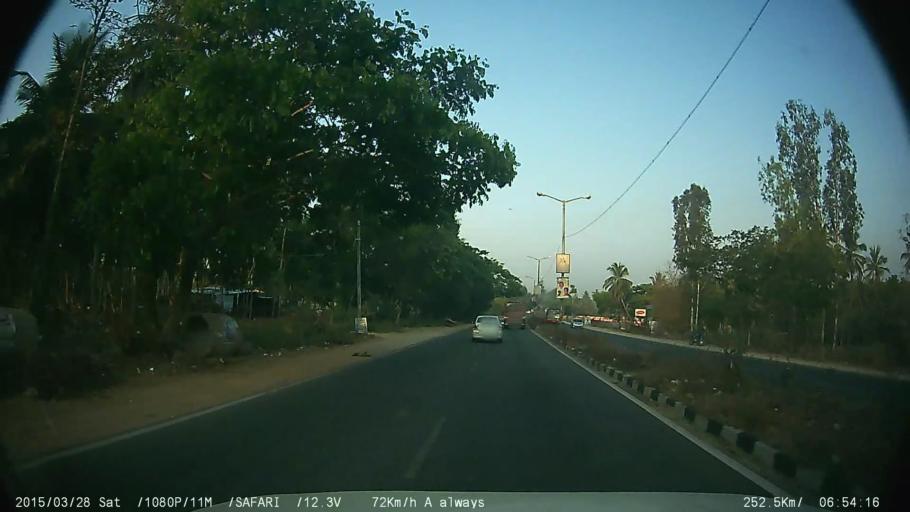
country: IN
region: Karnataka
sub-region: Mandya
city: Maddur
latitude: 12.5800
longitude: 77.0296
